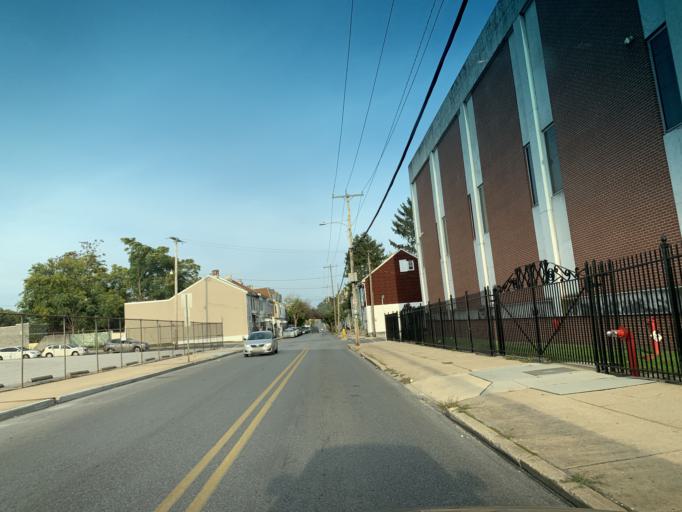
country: US
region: Pennsylvania
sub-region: York County
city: York
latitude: 39.9546
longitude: -76.7376
